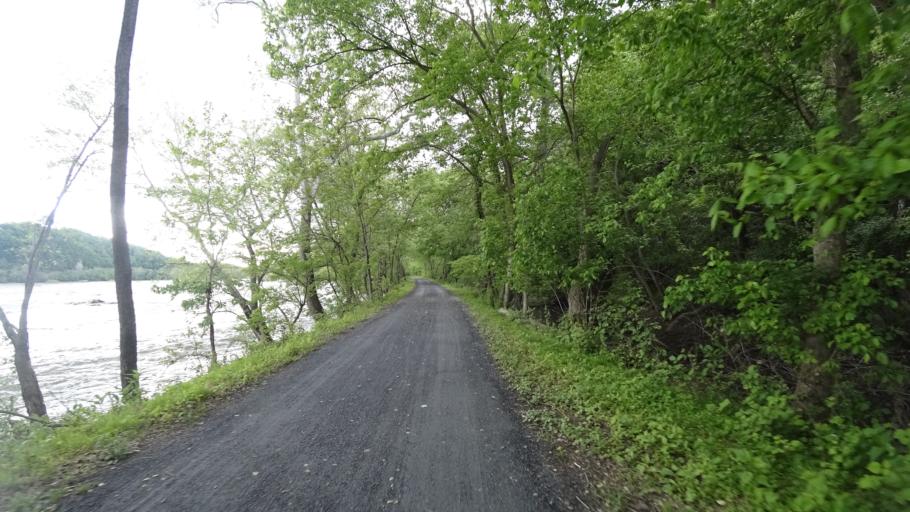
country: US
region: West Virginia
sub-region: Jefferson County
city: Bolivar
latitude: 39.3352
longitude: -77.7436
